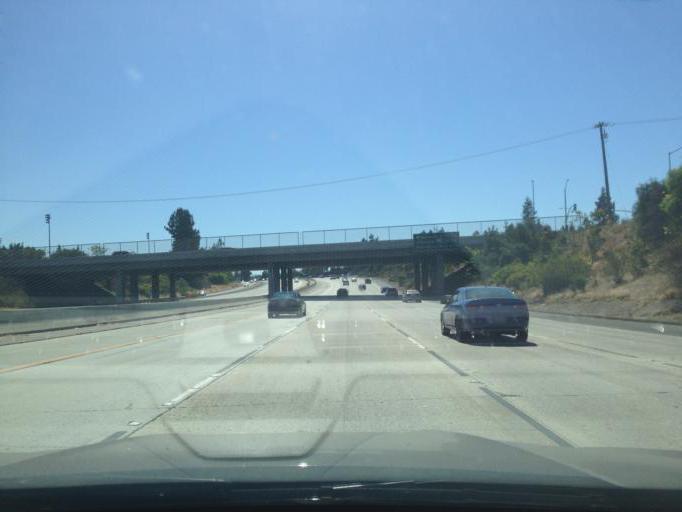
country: US
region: California
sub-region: Santa Clara County
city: Campbell
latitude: 37.3175
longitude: -121.9764
